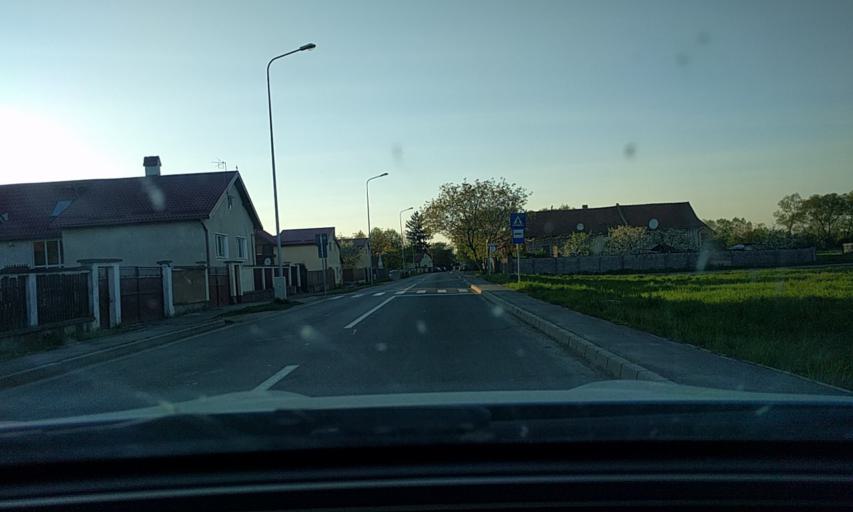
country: RO
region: Brasov
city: Brasov
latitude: 45.6928
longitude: 25.5633
